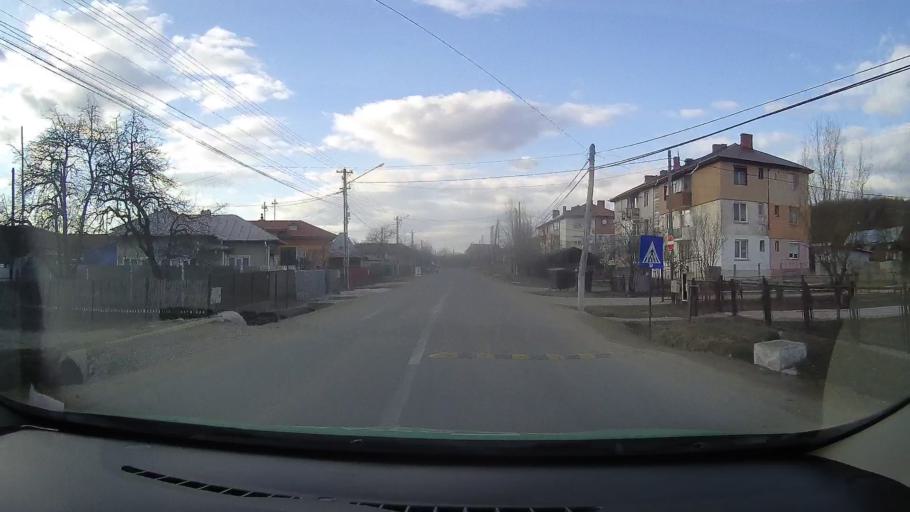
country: RO
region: Dambovita
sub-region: Comuna Gura Ocnitei
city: Gura Ocnitei
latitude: 44.9441
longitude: 25.5622
